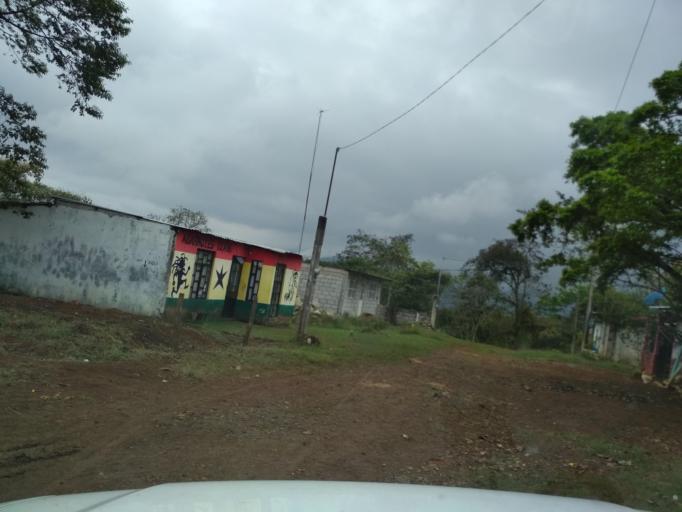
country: MX
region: Veracruz
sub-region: Cordoba
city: San Jose de Tapia
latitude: 18.8434
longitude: -96.9655
